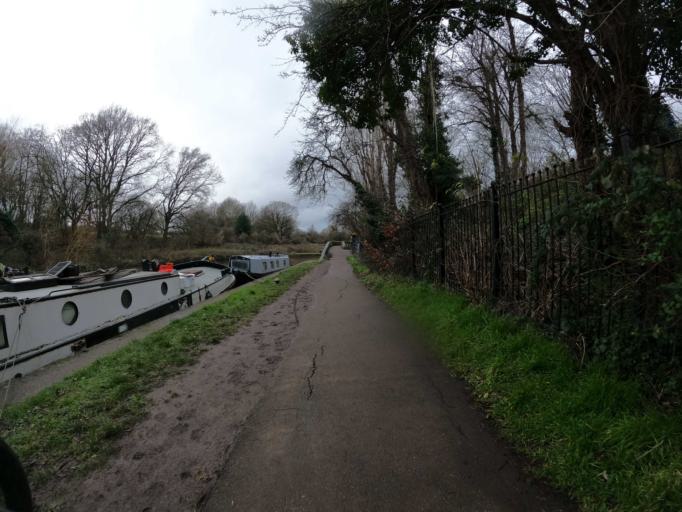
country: GB
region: England
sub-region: Greater London
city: Greenford
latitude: 51.5034
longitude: -0.3431
